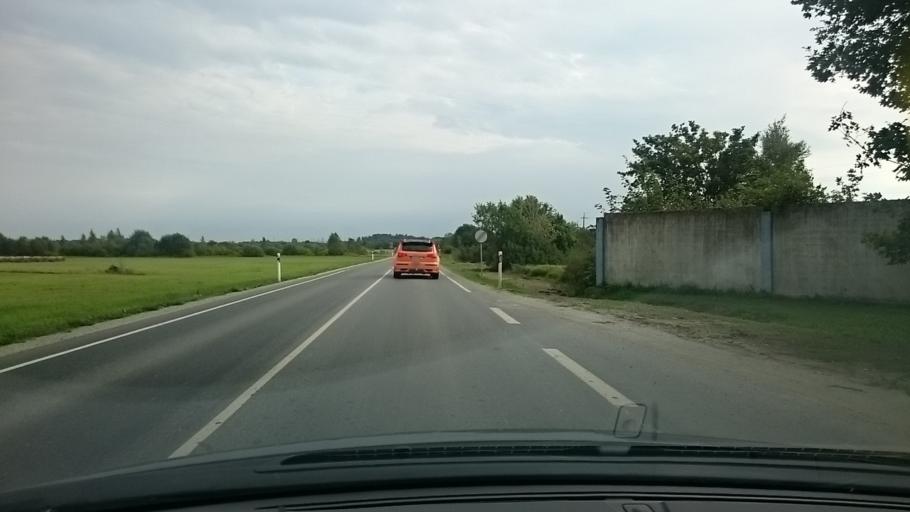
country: EE
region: Harju
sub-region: Harku vald
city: Tabasalu
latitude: 59.4071
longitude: 24.5468
